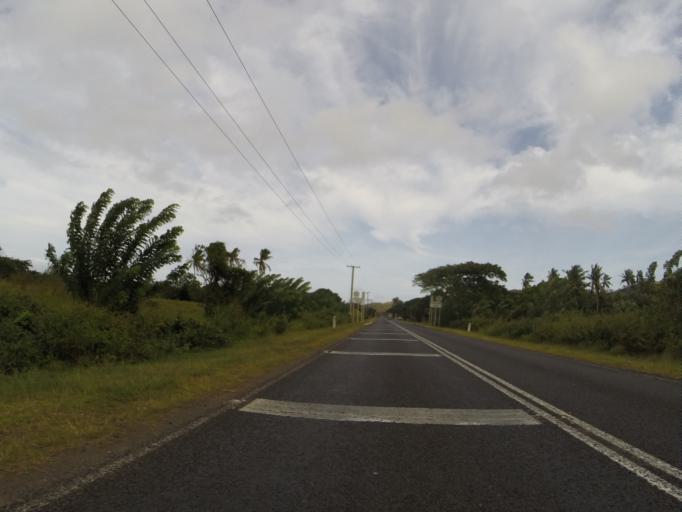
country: FJ
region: Western
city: Nadi
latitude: -18.1569
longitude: 177.4921
